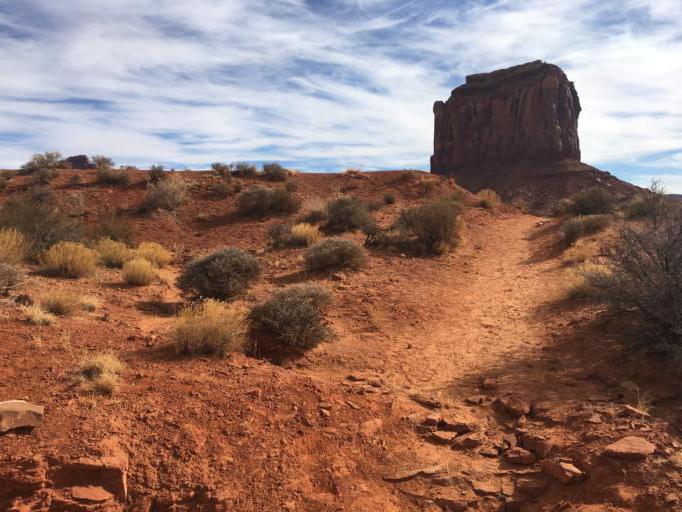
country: US
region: Arizona
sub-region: Navajo County
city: Kayenta
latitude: 36.9863
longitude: -110.0972
